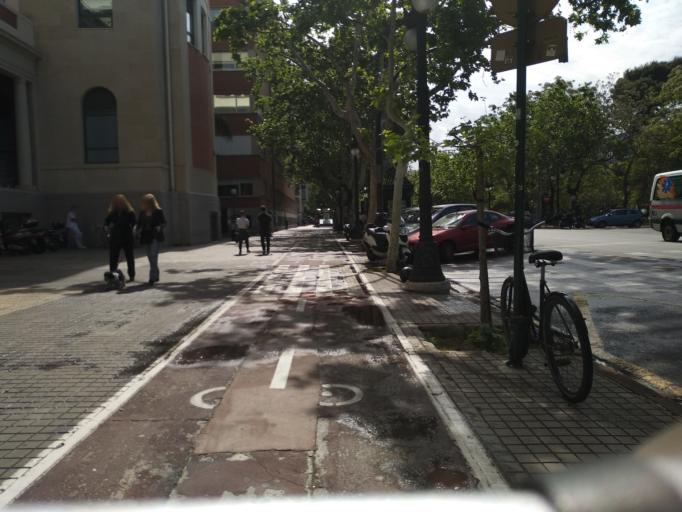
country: ES
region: Valencia
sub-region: Provincia de Valencia
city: Valencia
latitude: 39.4788
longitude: -0.3632
